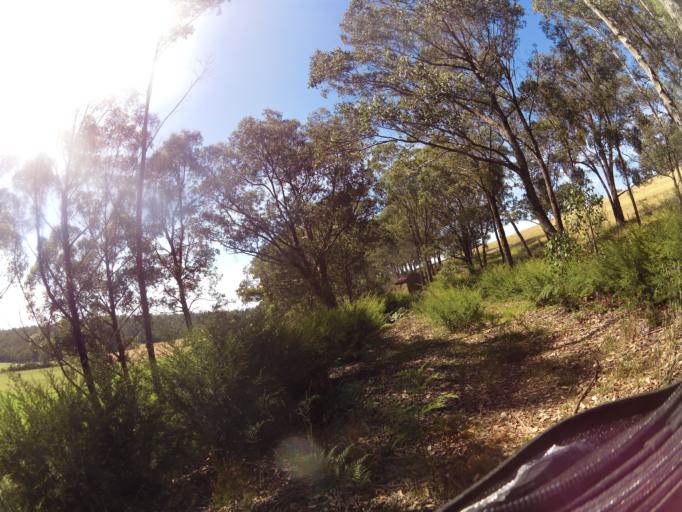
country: AU
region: Victoria
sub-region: East Gippsland
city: Lakes Entrance
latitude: -37.7333
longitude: 148.1622
